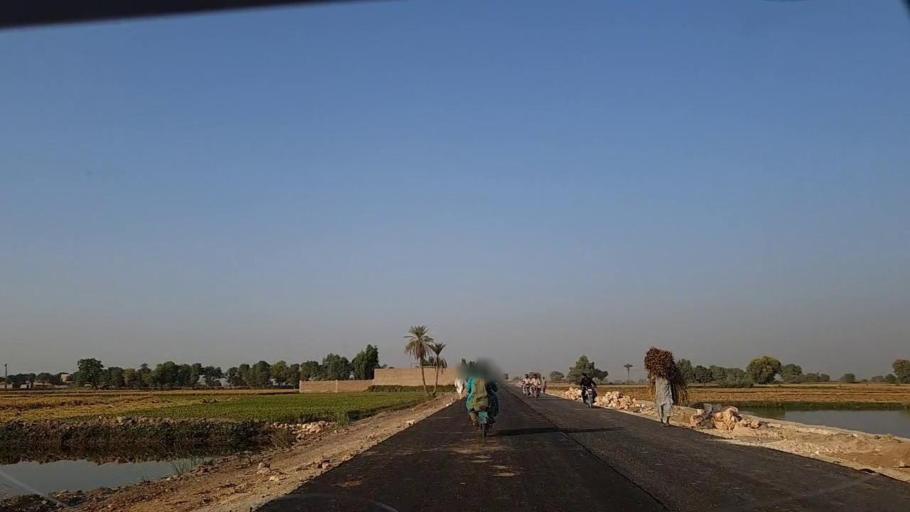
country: PK
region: Sindh
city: Rustam jo Goth
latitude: 27.9704
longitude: 68.8033
